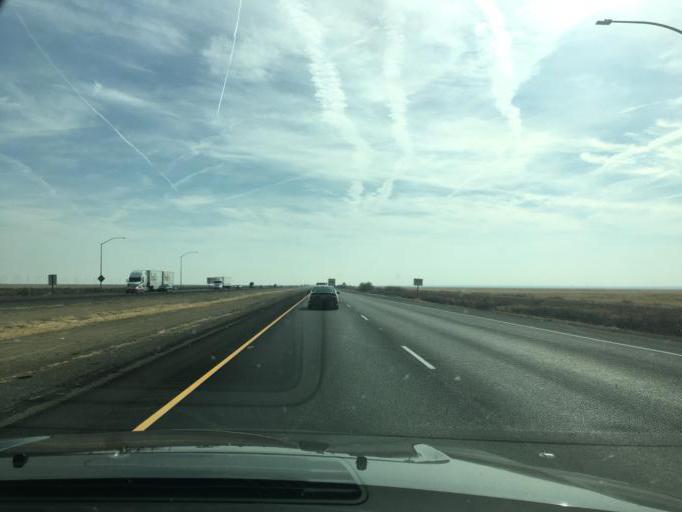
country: US
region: California
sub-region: Kern County
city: Lost Hills
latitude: 35.7299
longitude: -119.7380
